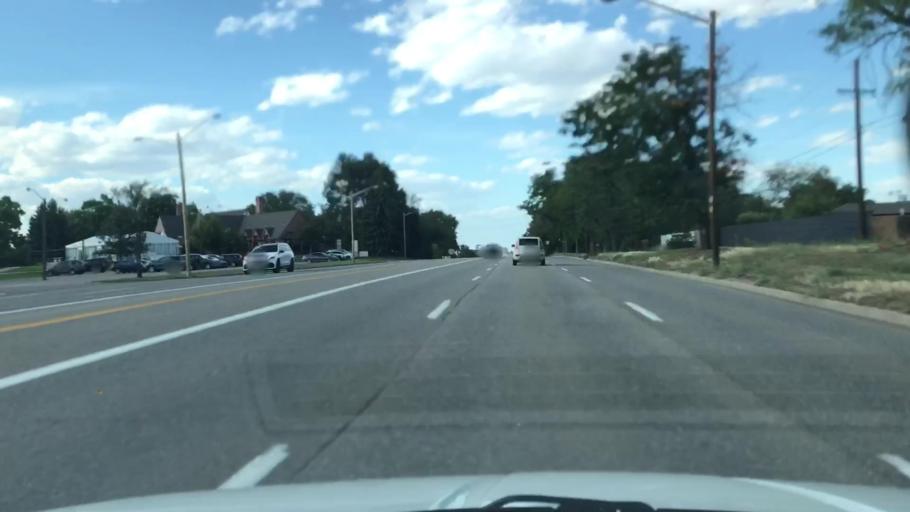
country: US
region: Colorado
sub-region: Arapahoe County
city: Cherry Hills Village
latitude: 39.6567
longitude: -104.9405
